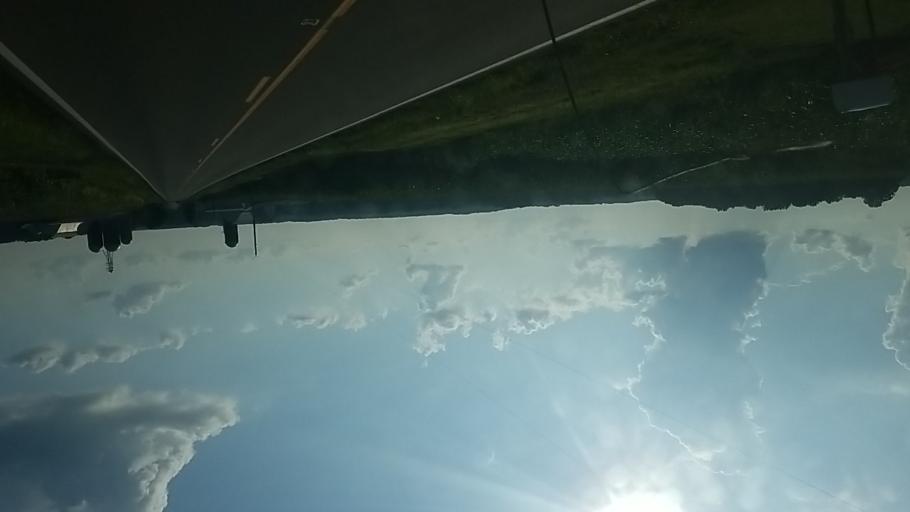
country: US
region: Ohio
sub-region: Wayne County
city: West Salem
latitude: 40.8880
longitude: -82.1331
